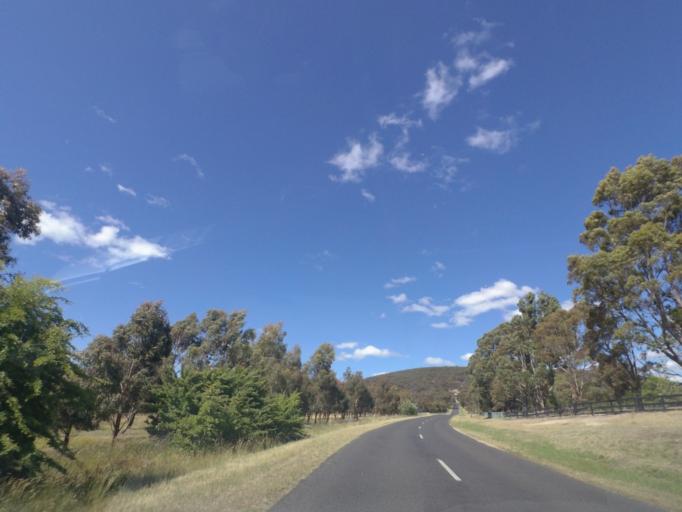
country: AU
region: Victoria
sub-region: Hume
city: Sunbury
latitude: -37.4298
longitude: 144.6105
